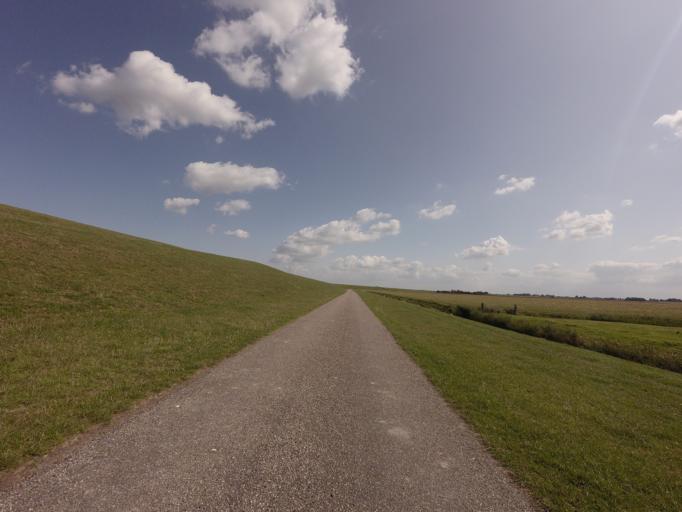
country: NL
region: Friesland
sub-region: Gemeente Ferwerderadiel
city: Hallum
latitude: 53.3241
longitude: 5.7230
